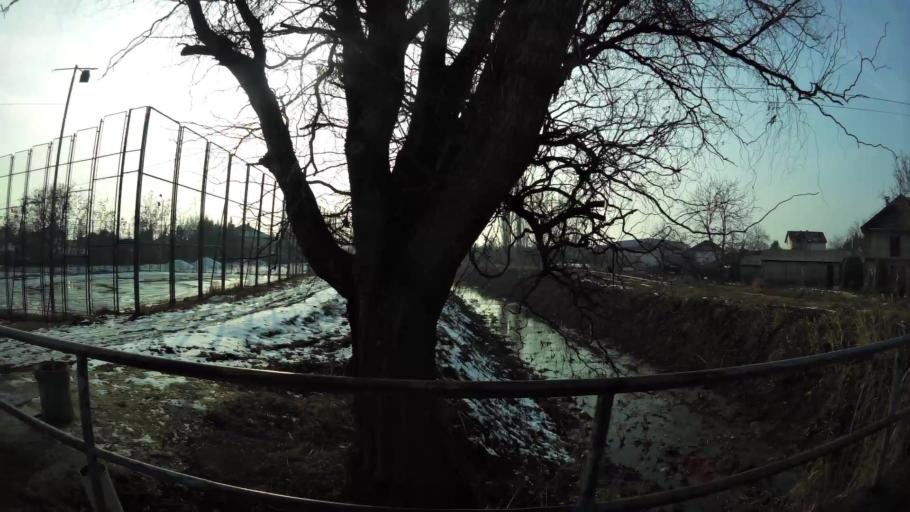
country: MK
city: Miladinovci
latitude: 41.9795
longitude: 21.6496
